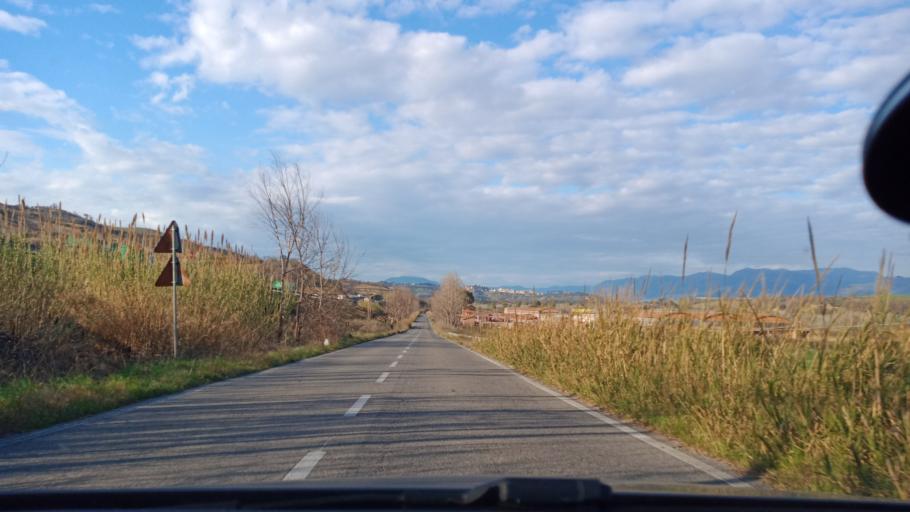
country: IT
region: Latium
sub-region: Citta metropolitana di Roma Capitale
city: Civitella San Paolo
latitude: 42.1889
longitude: 12.6038
